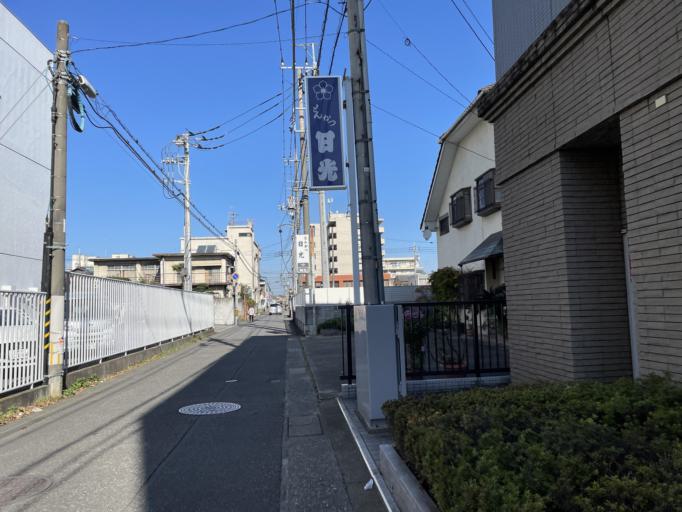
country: JP
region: Gunma
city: Tatebayashi
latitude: 36.2474
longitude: 139.5325
